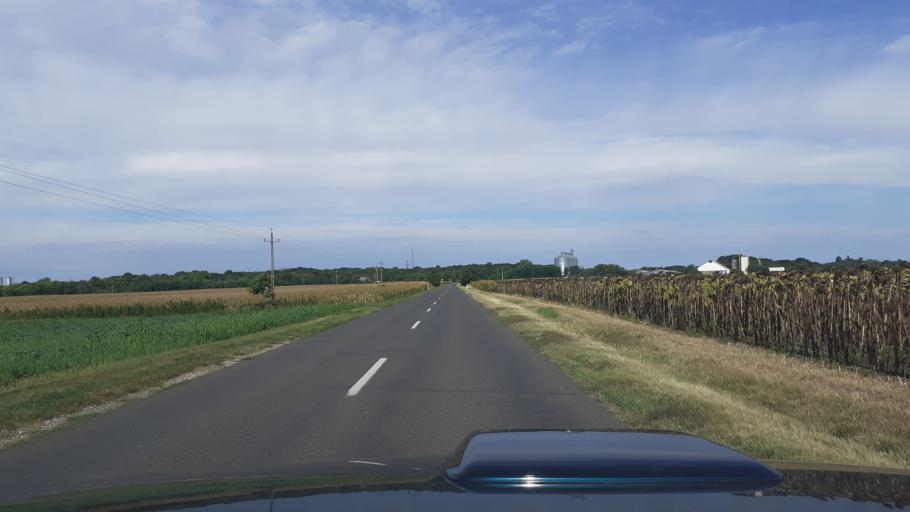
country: HU
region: Fejer
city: Pusztaszabolcs
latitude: 47.1269
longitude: 18.6815
